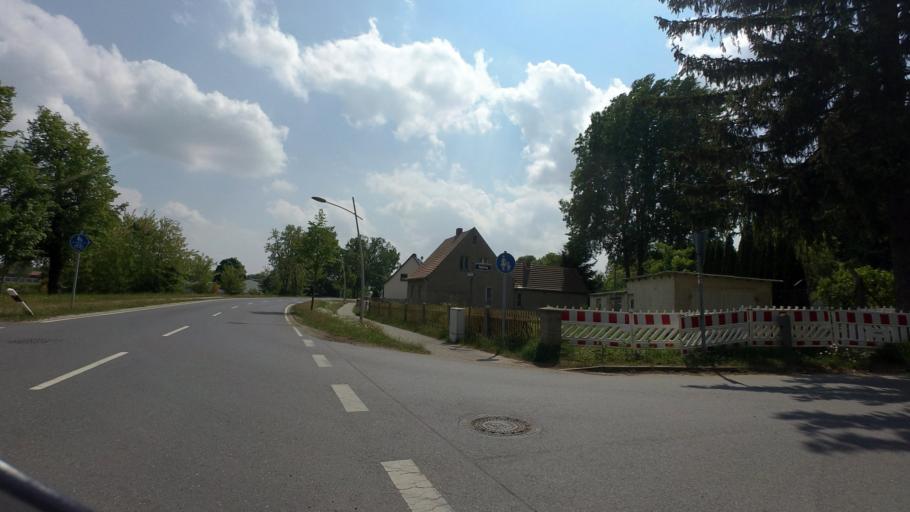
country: DE
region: Saxony
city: Niesky
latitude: 51.3038
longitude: 14.8278
